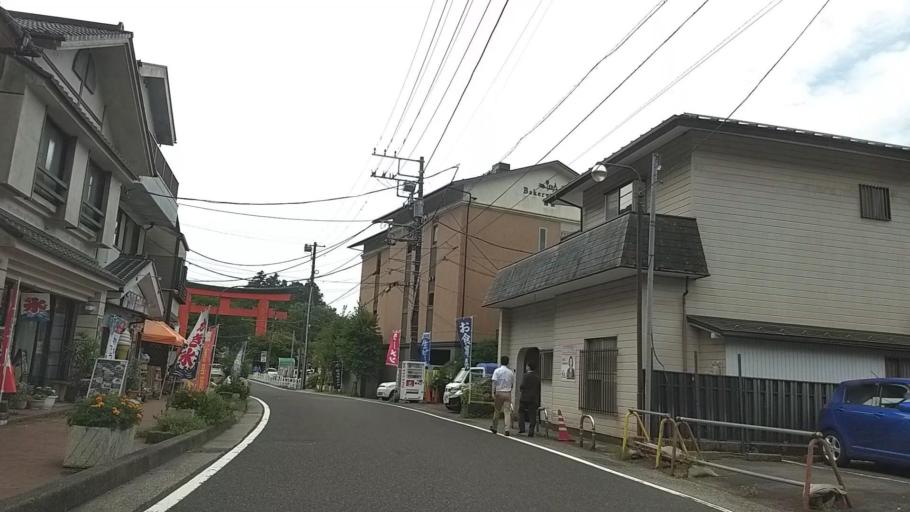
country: JP
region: Kanagawa
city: Hakone
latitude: 35.2022
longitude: 139.0313
